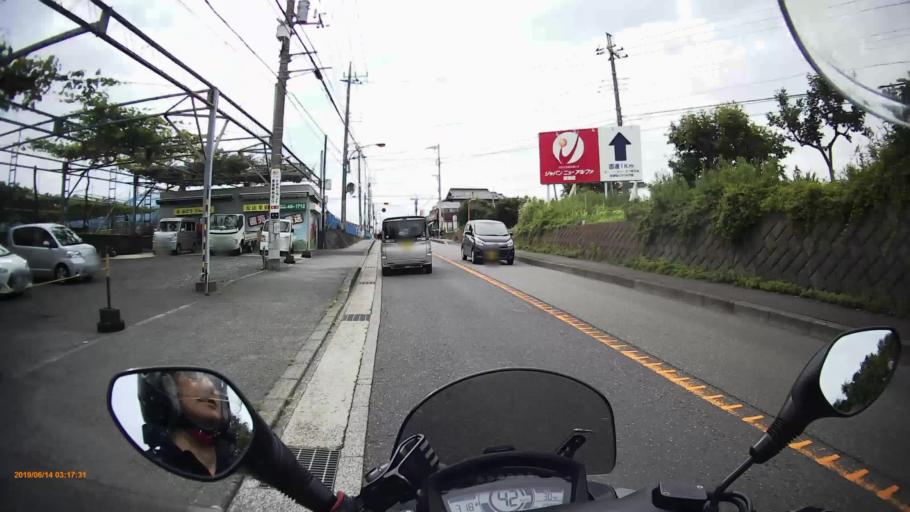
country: JP
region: Kanagawa
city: Minami-rinkan
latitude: 35.4174
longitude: 139.4588
